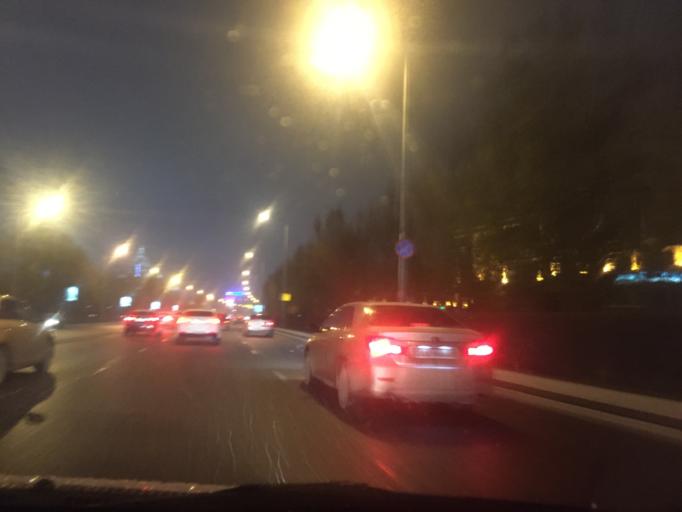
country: KZ
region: Astana Qalasy
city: Astana
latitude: 51.1514
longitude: 71.4126
